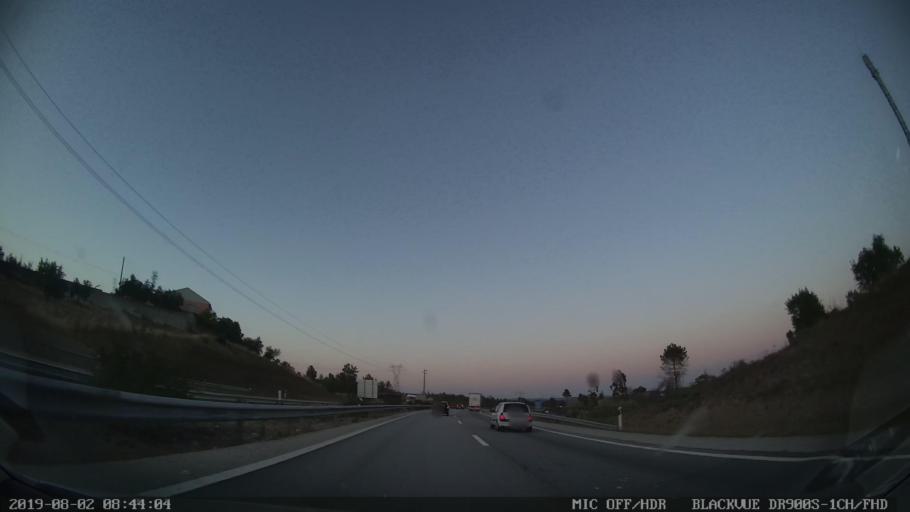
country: PT
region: Santarem
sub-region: Abrantes
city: Abrantes
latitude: 39.4912
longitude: -8.2064
